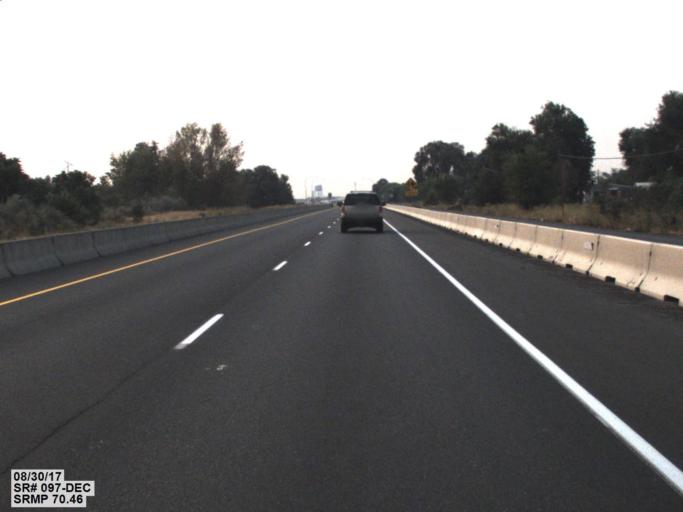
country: US
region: Washington
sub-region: Yakima County
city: Wapato
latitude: 46.4664
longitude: -120.4383
